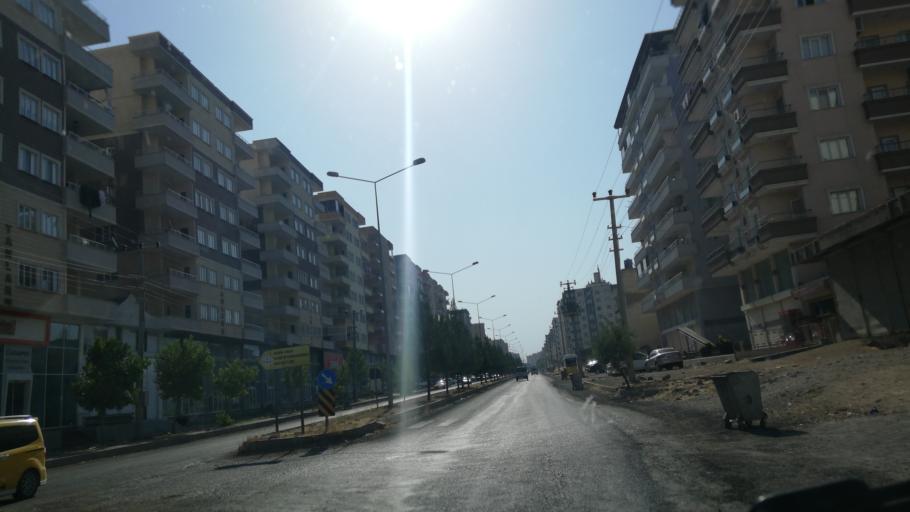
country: TR
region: Mardin
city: Midyat
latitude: 37.4348
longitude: 41.3254
